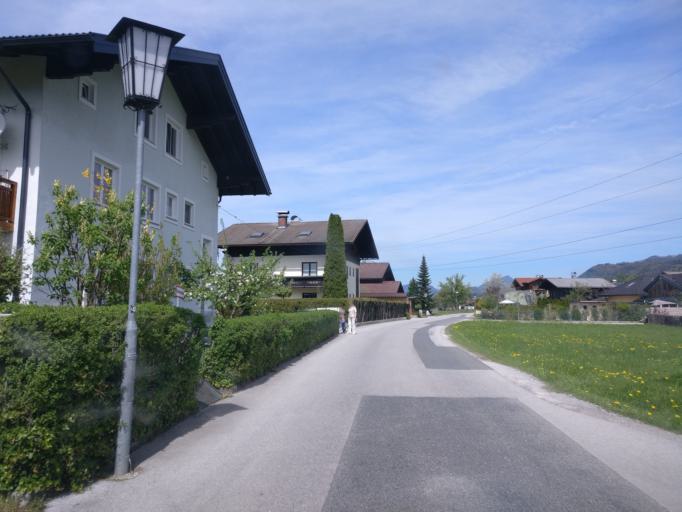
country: AT
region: Salzburg
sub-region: Politischer Bezirk Hallein
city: Kuchl
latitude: 47.6226
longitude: 13.1550
